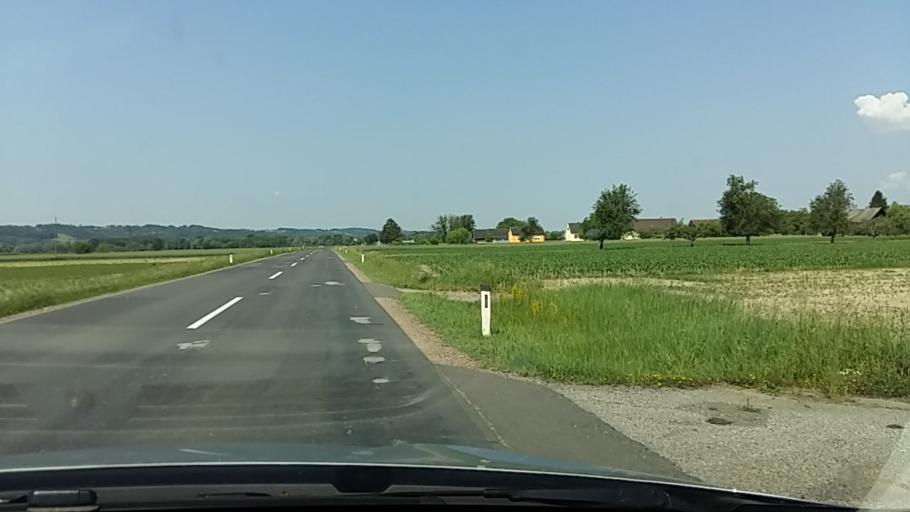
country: AT
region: Burgenland
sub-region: Politischer Bezirk Jennersdorf
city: Heiligenkreuz im Lafnitztal
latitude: 46.9829
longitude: 16.2612
